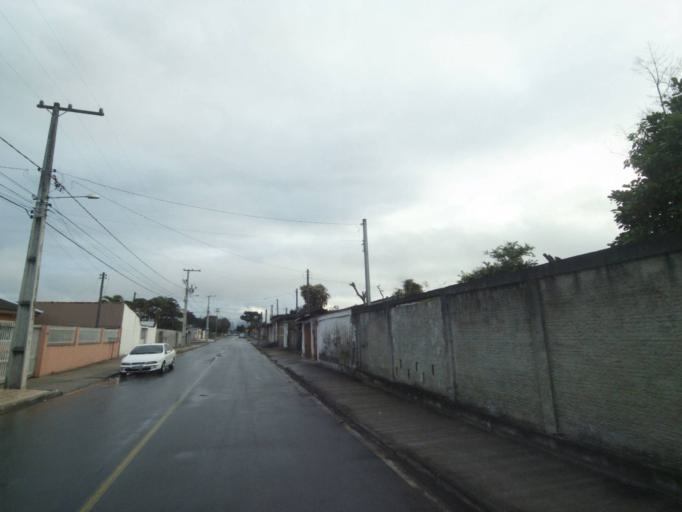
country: BR
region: Parana
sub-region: Paranagua
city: Paranagua
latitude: -25.5721
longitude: -48.5709
